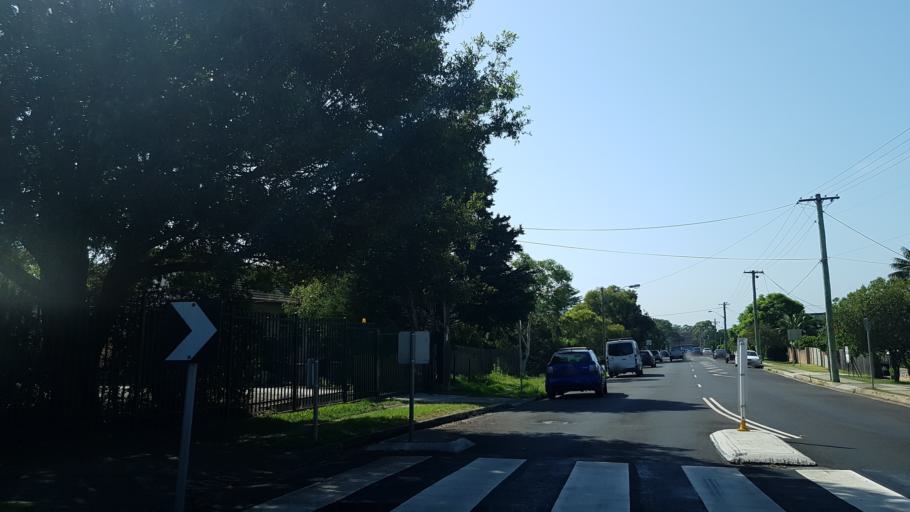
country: AU
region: New South Wales
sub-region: Warringah
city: Dee Why
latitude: -33.7415
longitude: 151.2912
